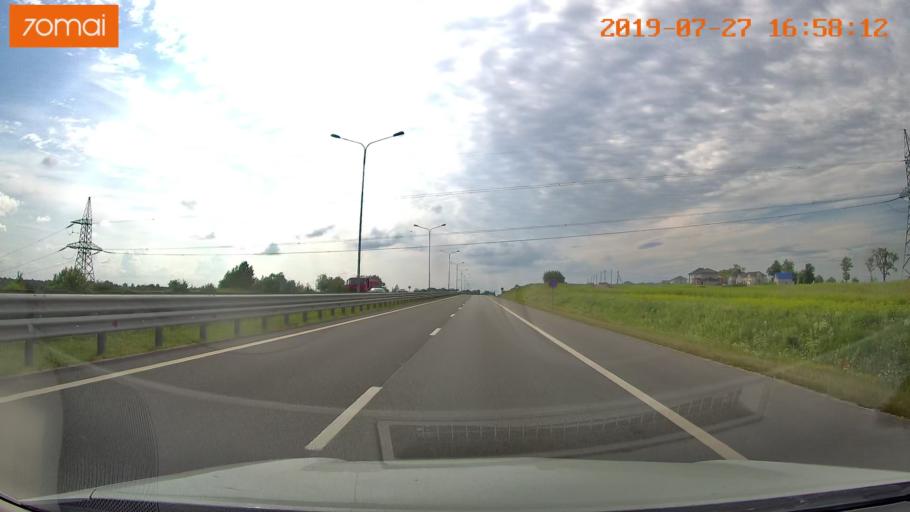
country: RU
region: Kaliningrad
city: Bol'shoe Isakovo
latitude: 54.7012
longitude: 20.6888
